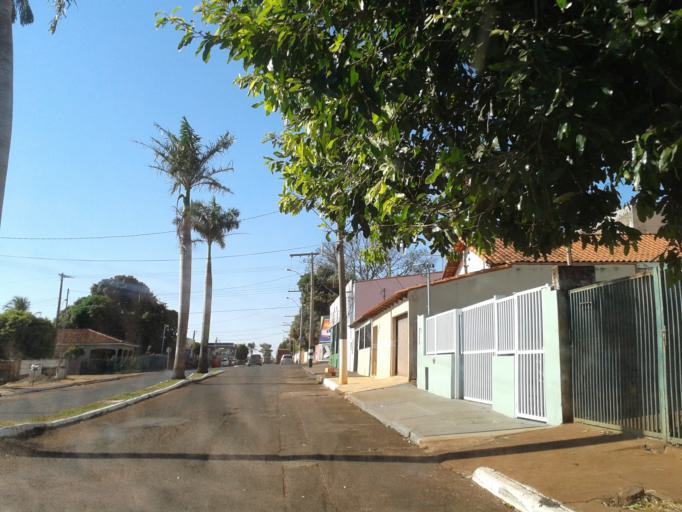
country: BR
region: Minas Gerais
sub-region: Capinopolis
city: Capinopolis
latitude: -18.6860
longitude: -49.5682
